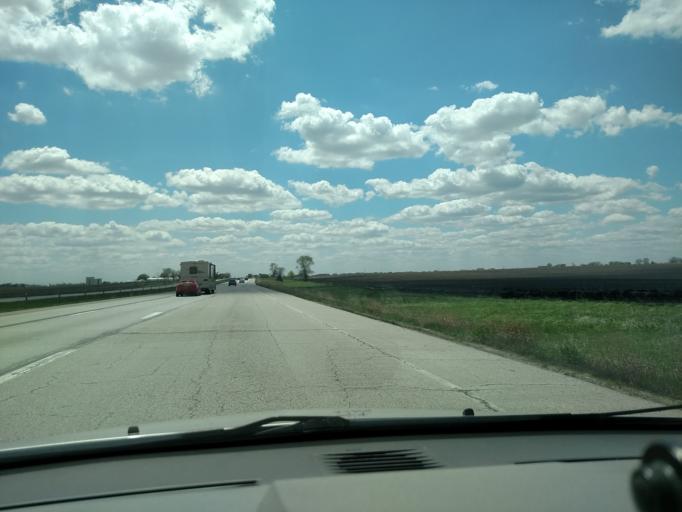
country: US
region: Iowa
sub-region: Polk County
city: Ankeny
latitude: 41.7877
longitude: -93.5707
